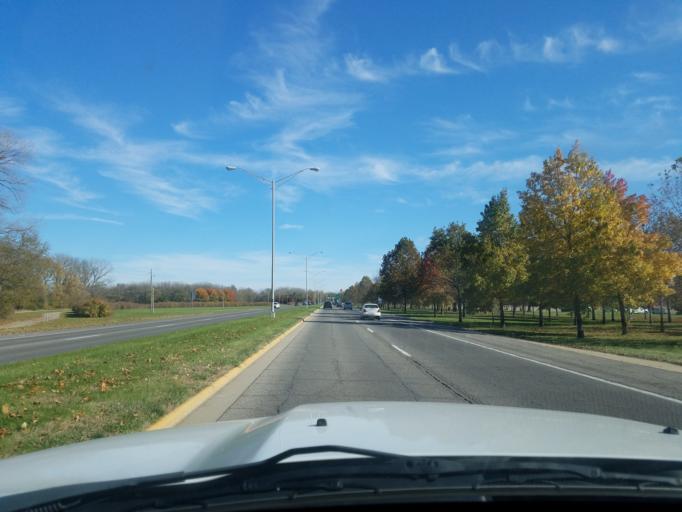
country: US
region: Indiana
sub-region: Bartholomew County
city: Columbus
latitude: 39.1998
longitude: -85.9410
